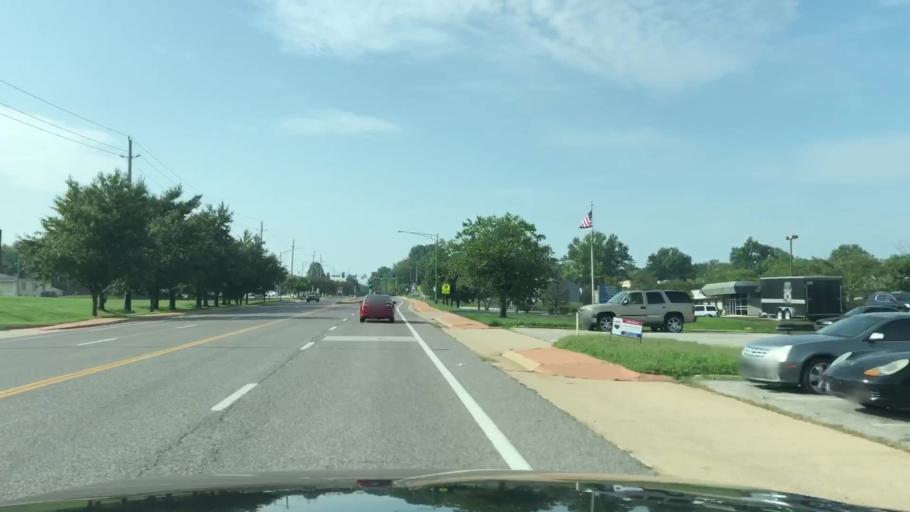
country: US
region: Missouri
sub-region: Saint Louis County
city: Woodson Terrace
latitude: 38.7295
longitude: -90.3578
